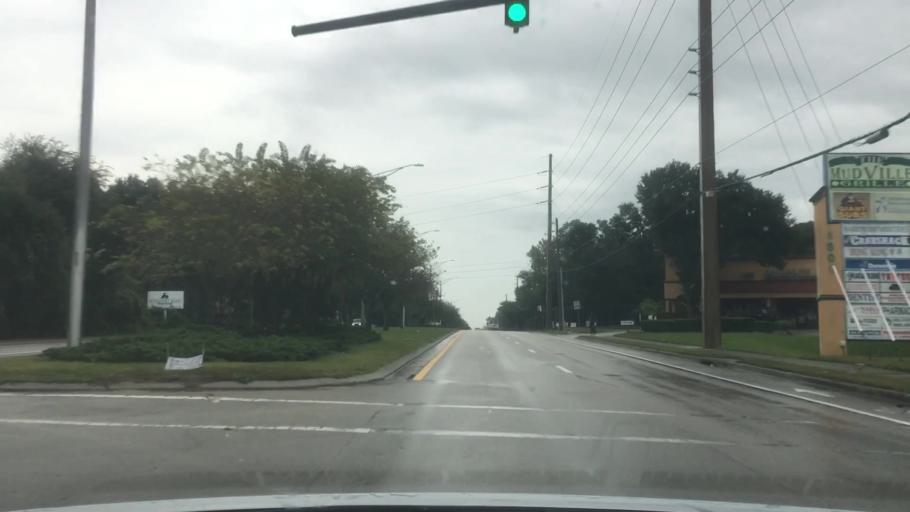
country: US
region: Florida
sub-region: Duval County
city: Jacksonville
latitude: 30.3427
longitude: -81.5372
